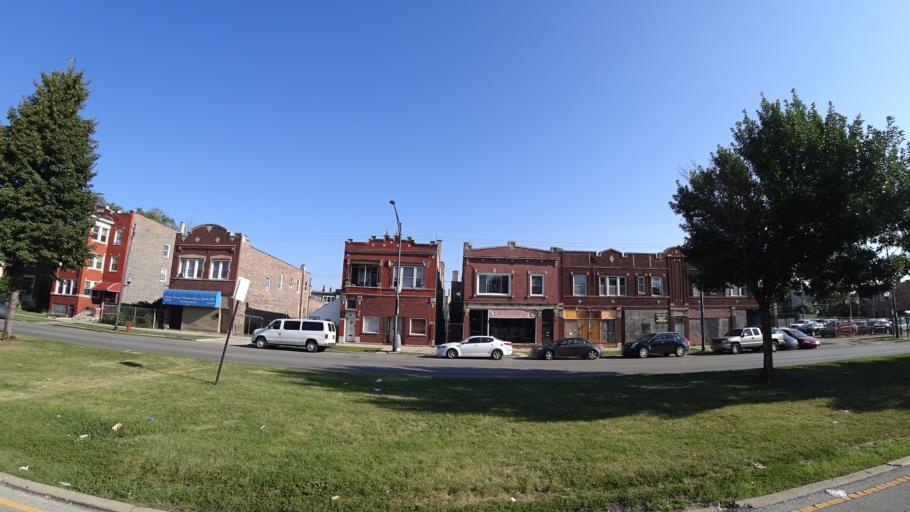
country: US
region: Illinois
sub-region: Cook County
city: Cicero
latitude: 41.8514
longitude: -87.7307
